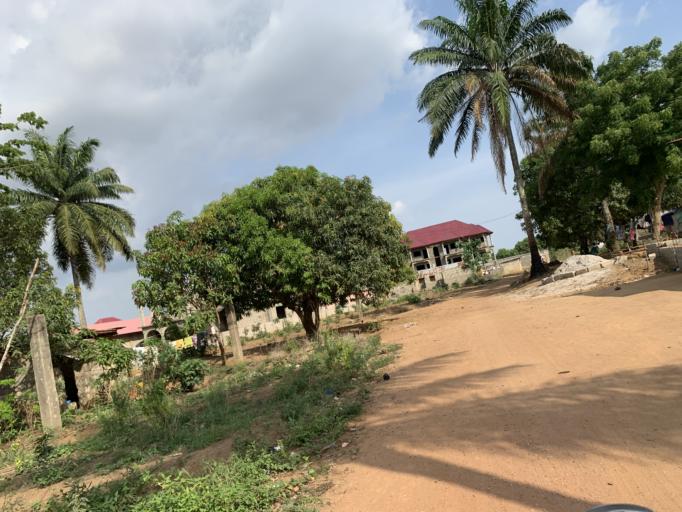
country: SL
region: Western Area
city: Waterloo
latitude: 8.3433
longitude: -13.0467
